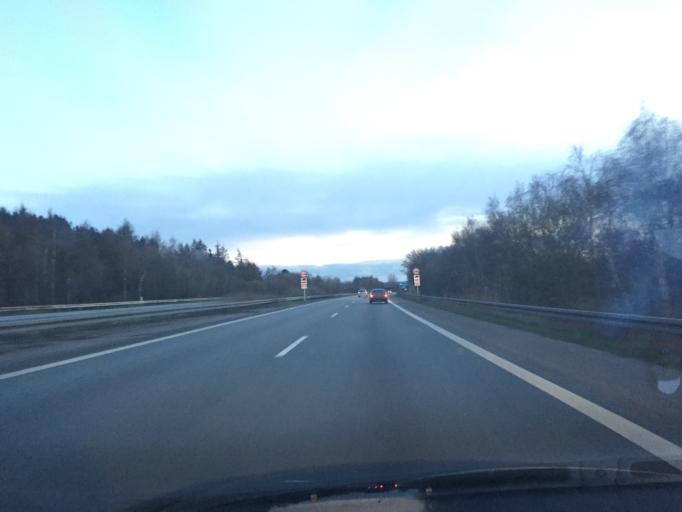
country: DK
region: Capital Region
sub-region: Fredensborg Kommune
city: Humlebaek
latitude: 55.9767
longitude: 12.5057
